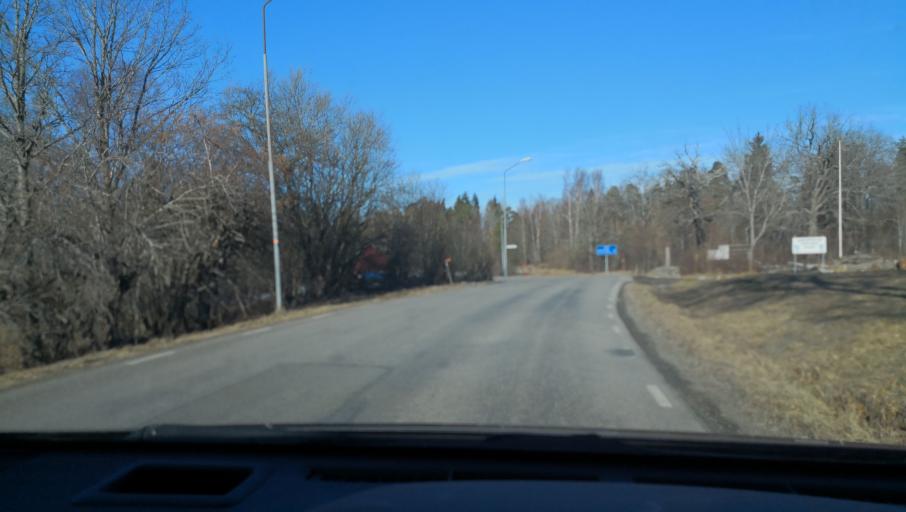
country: SE
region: Uppsala
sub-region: Osthammars Kommun
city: Osterbybruk
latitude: 60.2056
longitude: 17.8995
